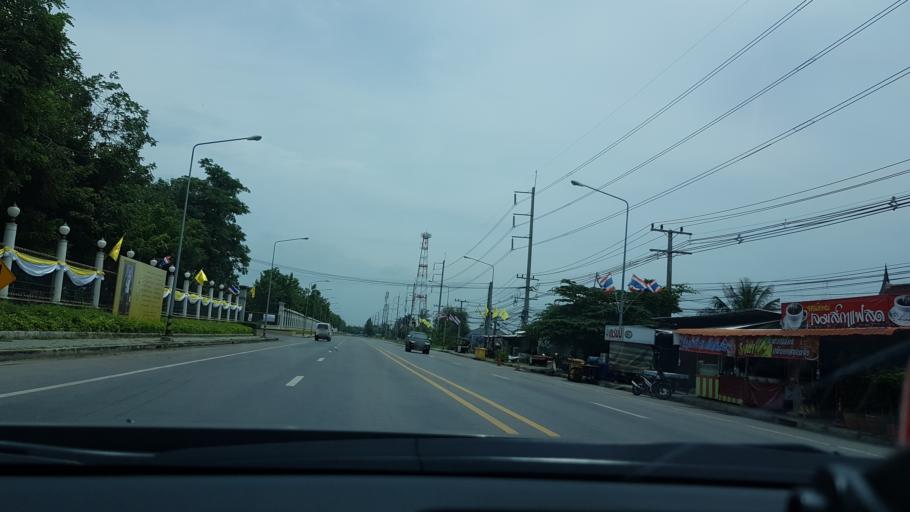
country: TH
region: Pathum Thani
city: Sam Khok
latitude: 14.1497
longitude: 100.5234
